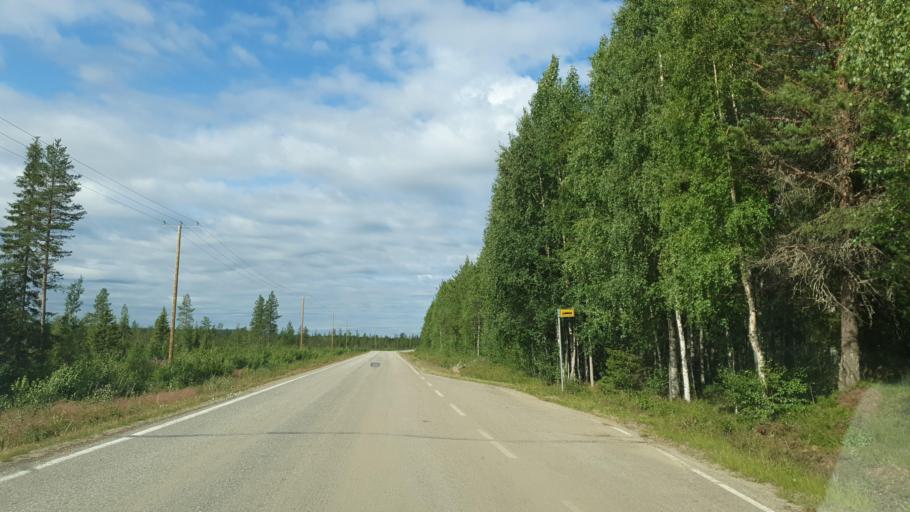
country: FI
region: Lapland
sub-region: Pohjois-Lappi
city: Sodankylae
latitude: 67.5258
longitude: 26.0007
